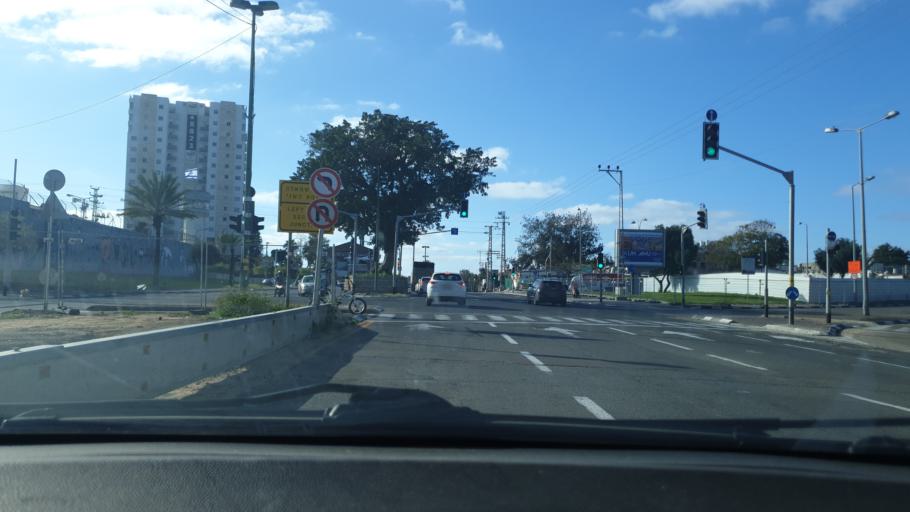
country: IL
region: Tel Aviv
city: Yafo
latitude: 32.0424
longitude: 34.7719
